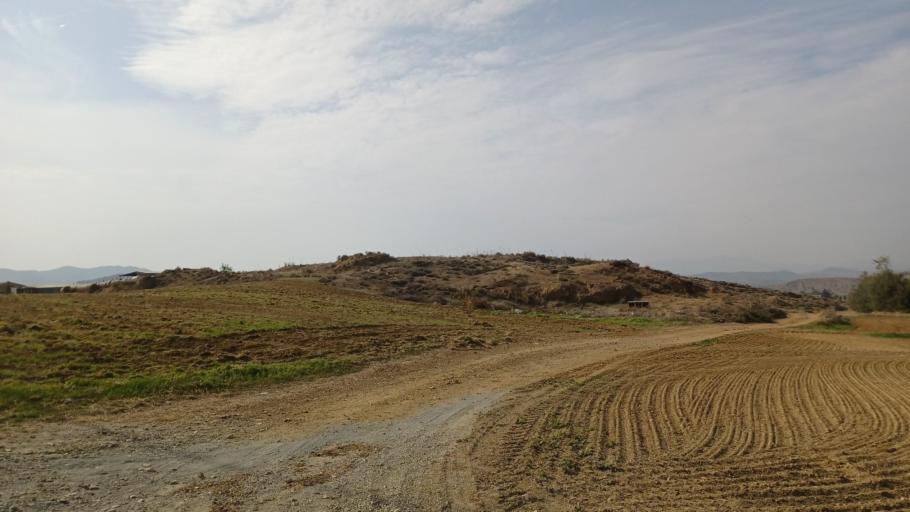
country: CY
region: Lefkosia
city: Lympia
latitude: 34.9788
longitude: 33.4530
